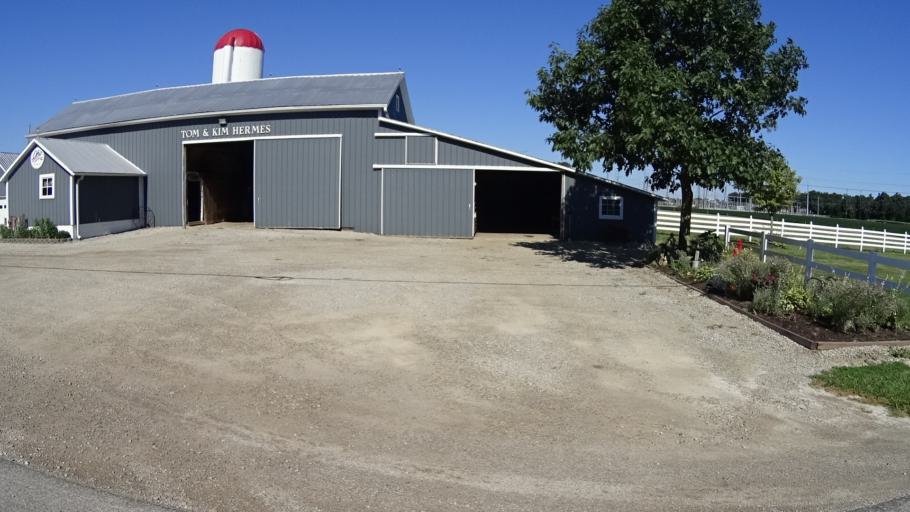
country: US
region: Ohio
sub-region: Erie County
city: Sandusky
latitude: 41.3722
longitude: -82.7250
